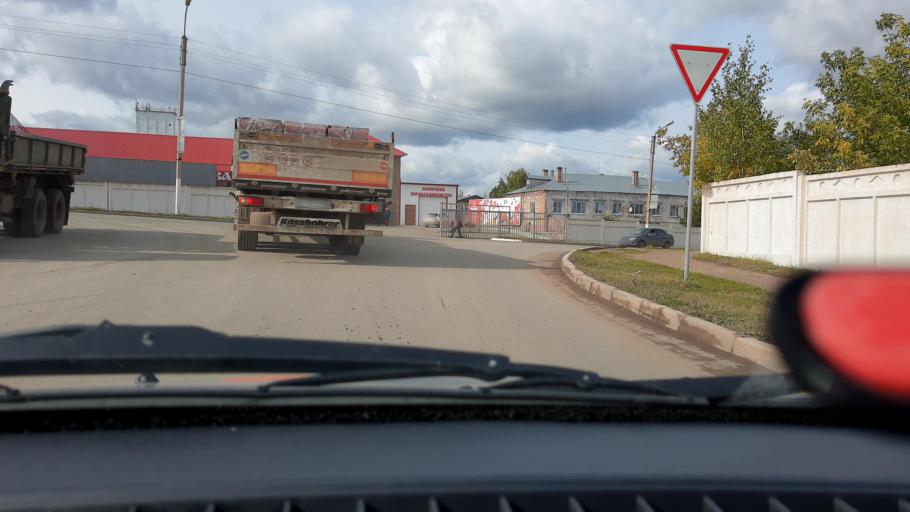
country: RU
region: Bashkortostan
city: Belebey
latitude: 54.0976
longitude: 54.1234
